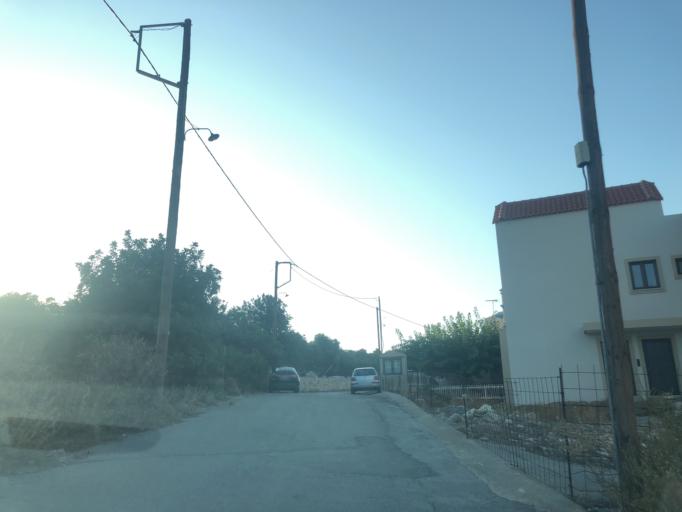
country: GR
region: Crete
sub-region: Nomos Rethymnis
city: Atsipopoulon
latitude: 35.3545
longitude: 24.3978
